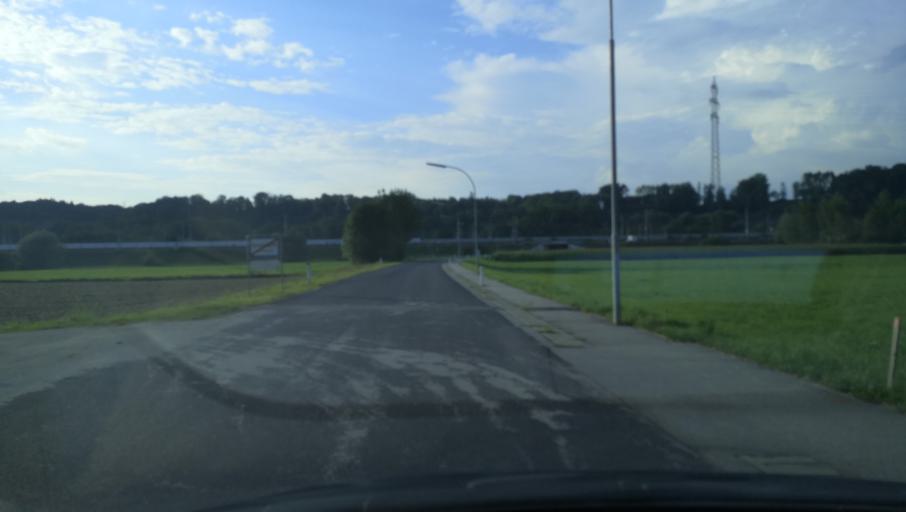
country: AT
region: Lower Austria
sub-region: Politischer Bezirk Amstetten
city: Amstetten
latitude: 48.1116
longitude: 14.8447
